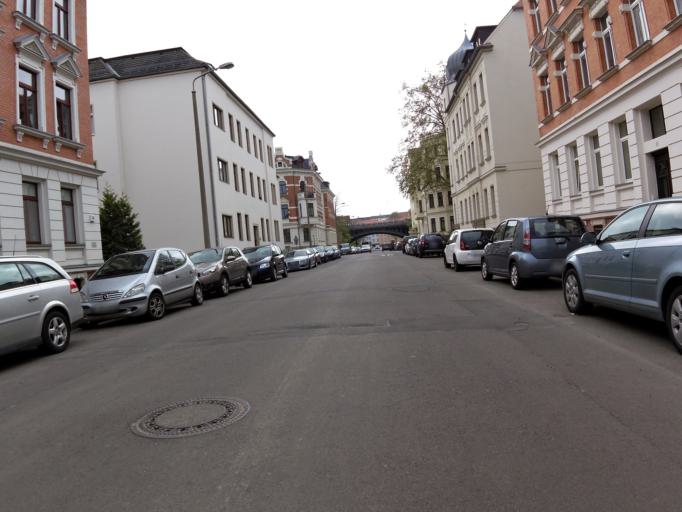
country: DE
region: Saxony
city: Leipzig
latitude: 51.3626
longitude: 12.3794
